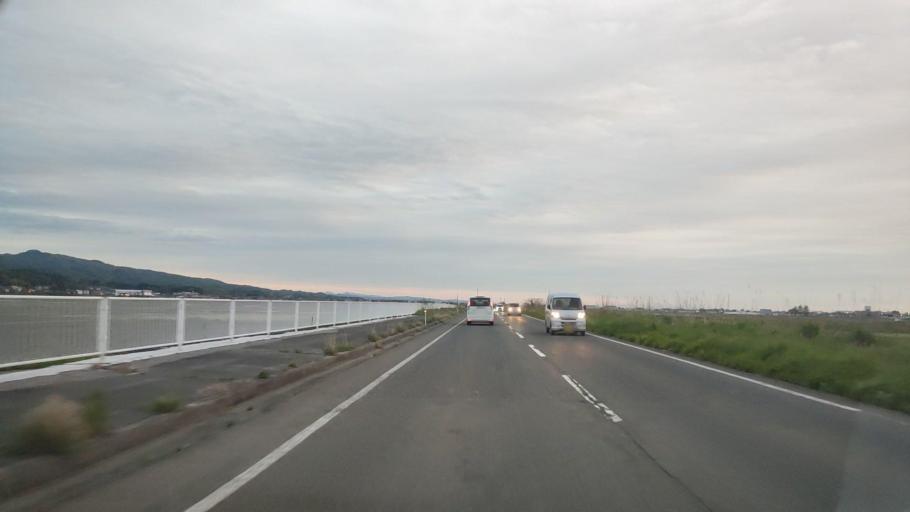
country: JP
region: Niigata
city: Niitsu-honcho
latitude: 37.7629
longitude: 139.0966
